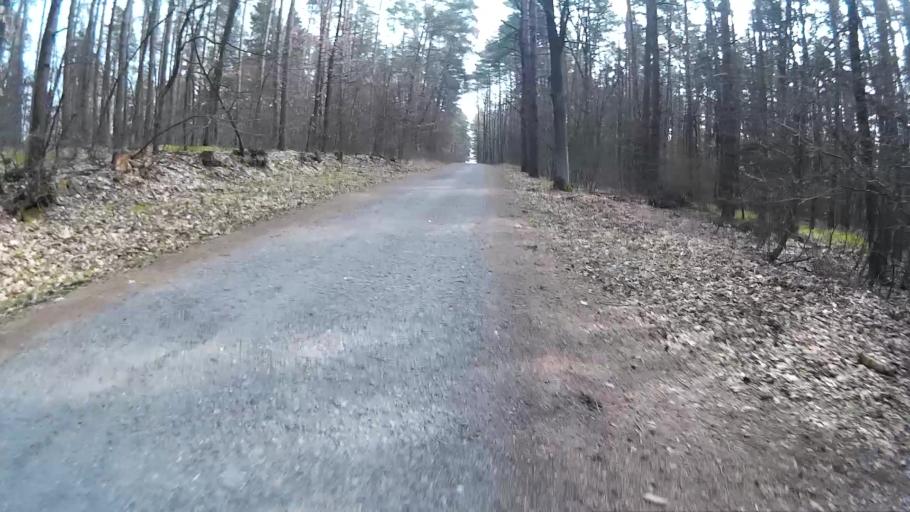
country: CZ
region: South Moravian
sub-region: Mesto Brno
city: Mokra Hora
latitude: 49.2601
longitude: 16.6129
